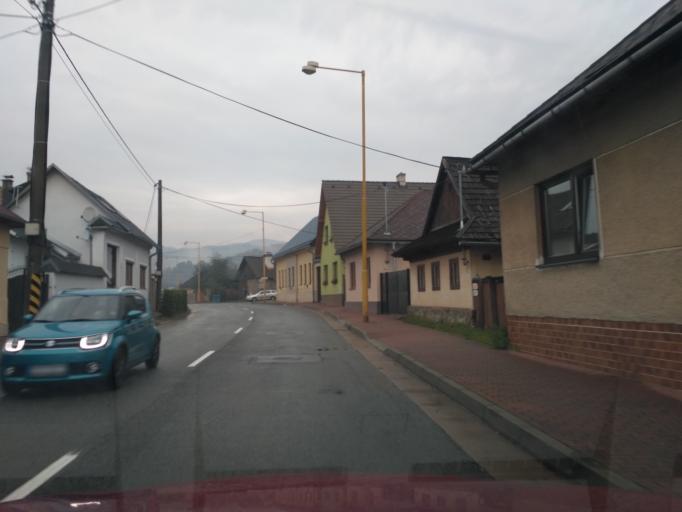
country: SK
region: Kosicky
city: Medzev
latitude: 48.7038
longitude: 20.8865
